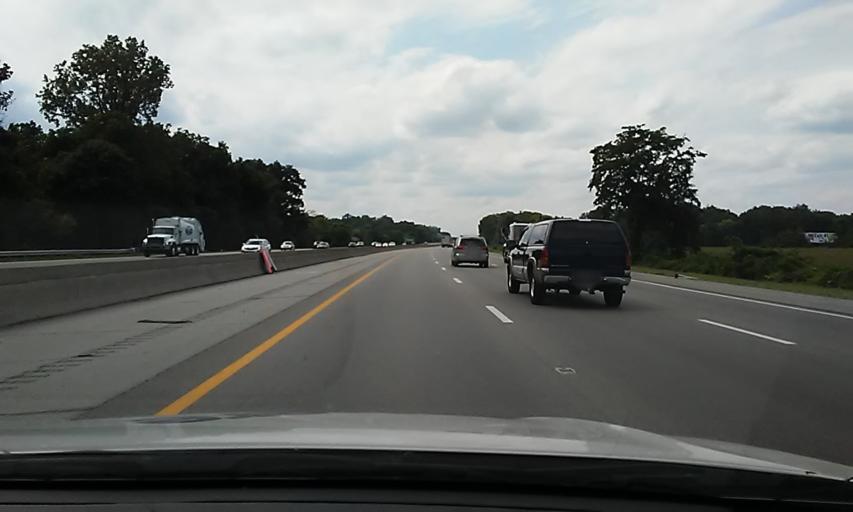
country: US
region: Ohio
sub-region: Clark County
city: Crystal Lakes
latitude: 39.8645
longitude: -84.0082
